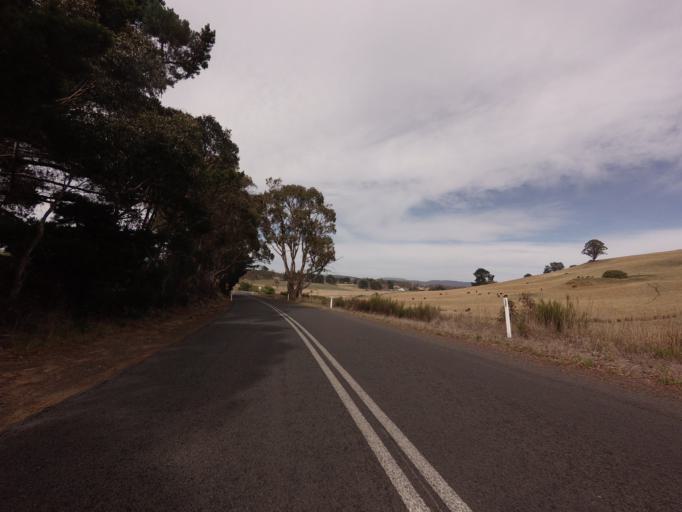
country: AU
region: Tasmania
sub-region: Sorell
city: Sorell
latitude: -42.4281
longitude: 147.4664
